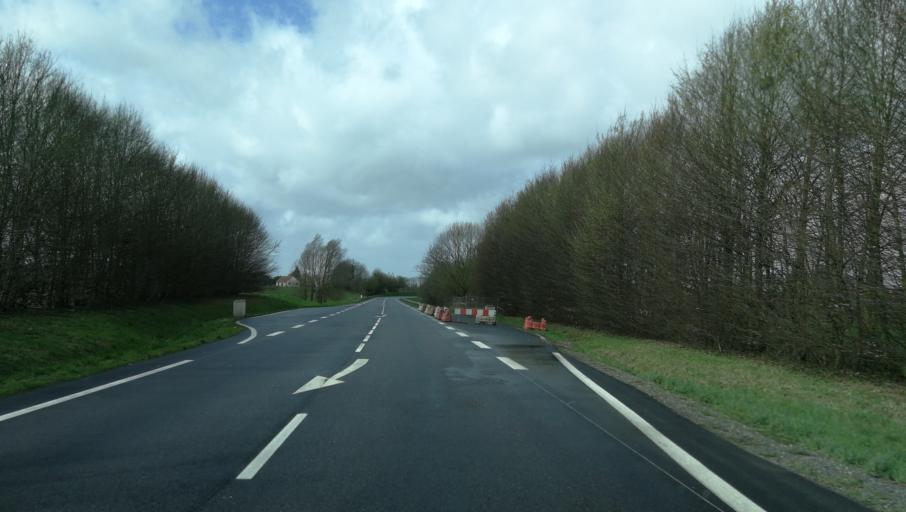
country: FR
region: Haute-Normandie
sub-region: Departement de l'Eure
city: Beuzeville
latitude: 49.3147
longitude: 0.3829
